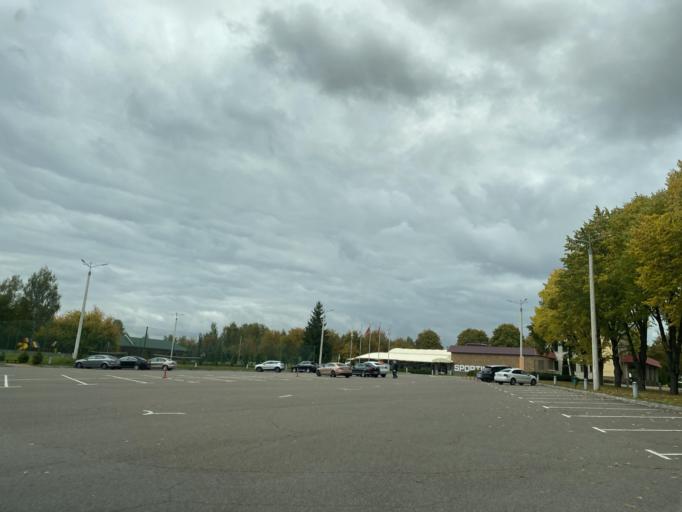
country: BY
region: Minsk
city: Lyeskawka
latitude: 53.9540
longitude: 27.7129
